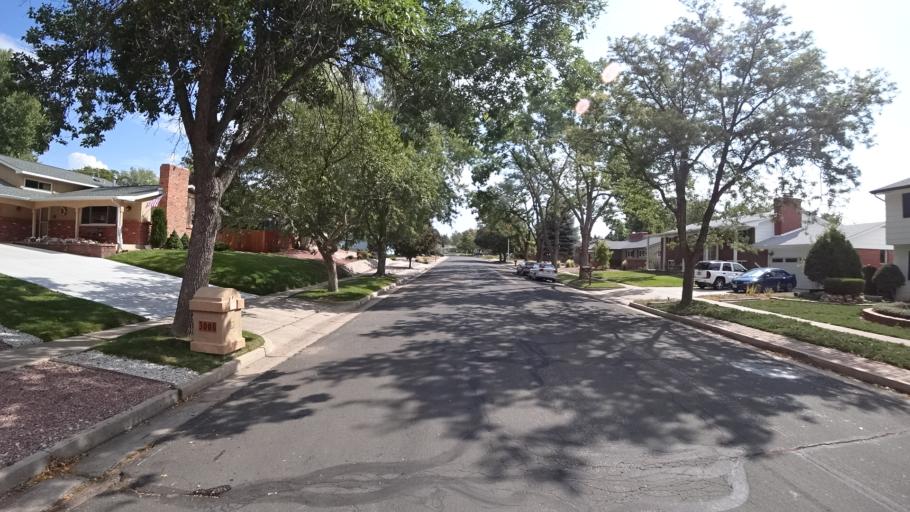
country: US
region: Colorado
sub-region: El Paso County
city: Colorado Springs
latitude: 38.8669
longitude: -104.7730
